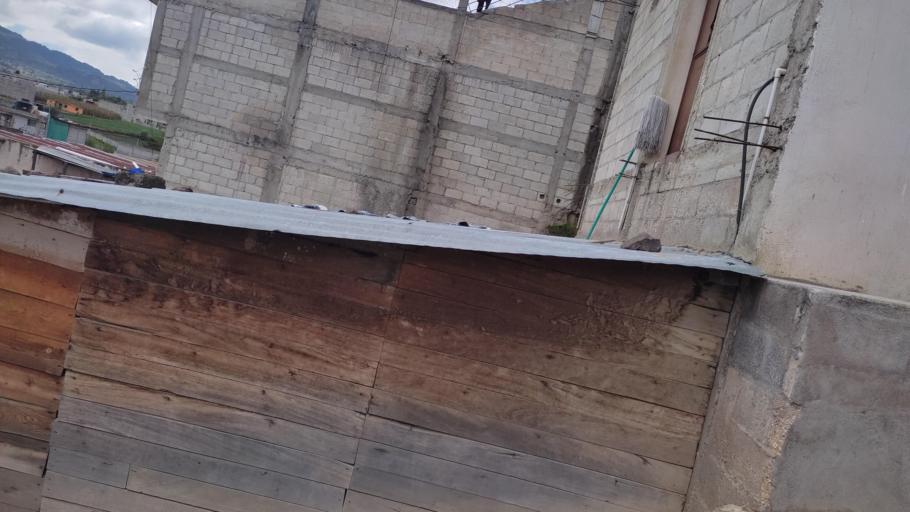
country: GT
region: Quetzaltenango
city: Quetzaltenango
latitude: 14.8568
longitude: -91.5281
